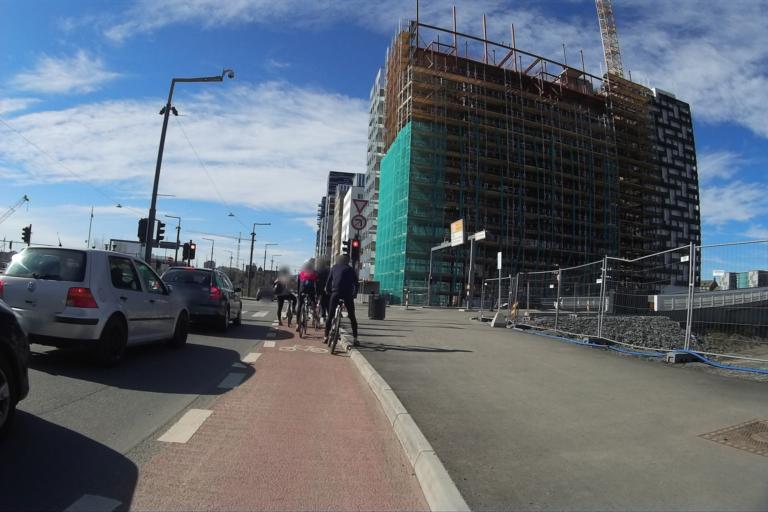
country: NO
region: Oslo
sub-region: Oslo
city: Oslo
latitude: 59.9067
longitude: 10.7627
